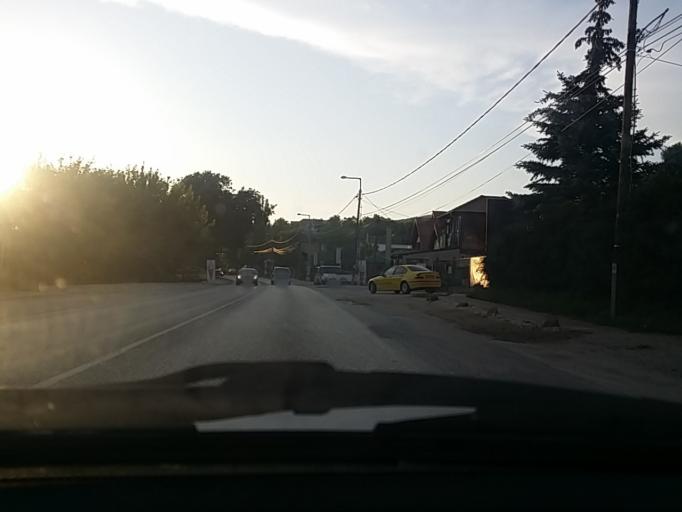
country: HU
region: Pest
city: Urom
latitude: 47.5855
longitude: 18.9975
